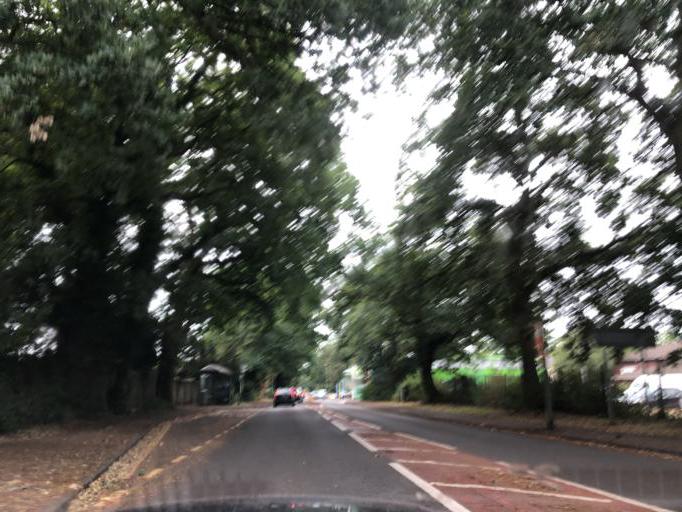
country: GB
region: England
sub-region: Hampshire
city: Farnborough
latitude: 51.2879
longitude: -0.7254
